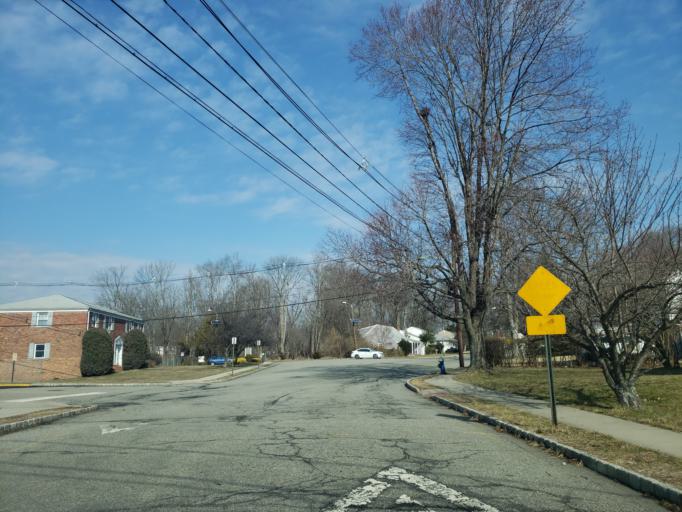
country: US
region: New Jersey
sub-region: Essex County
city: West Orange
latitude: 40.8062
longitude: -74.2576
